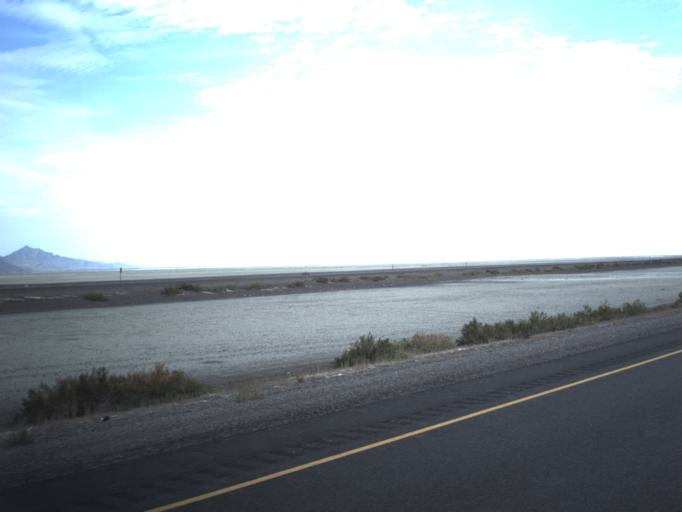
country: US
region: Utah
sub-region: Tooele County
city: Wendover
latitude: 40.7406
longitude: -113.9521
